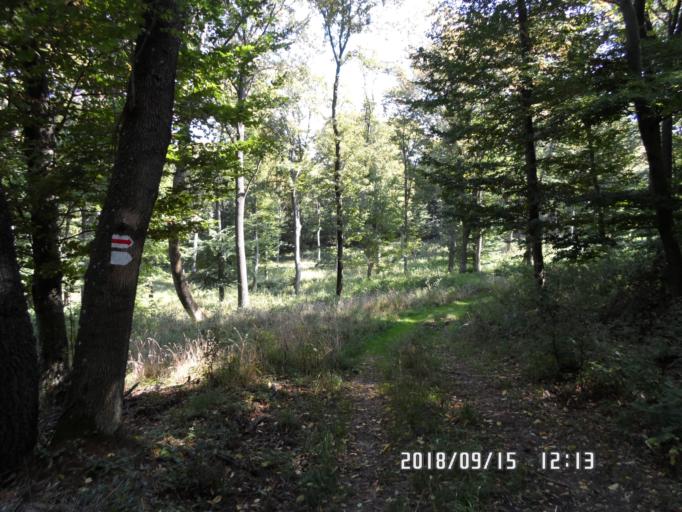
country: HU
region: Veszprem
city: Cseteny
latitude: 47.2500
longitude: 17.9696
